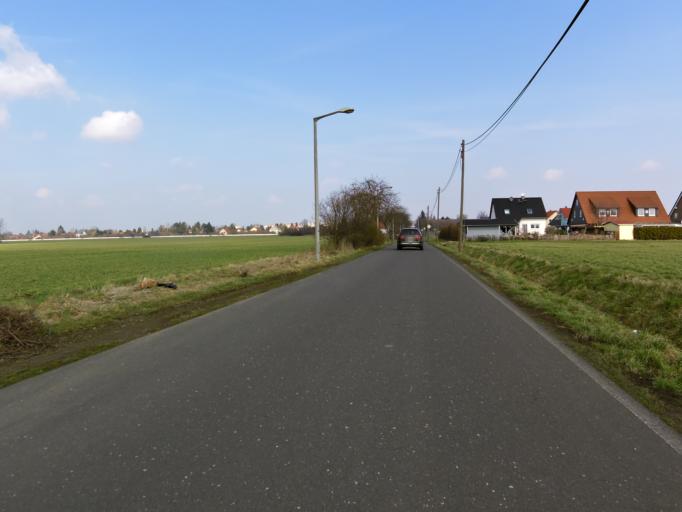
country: DE
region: Saxony
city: Markranstadt
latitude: 51.3045
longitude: 12.2931
